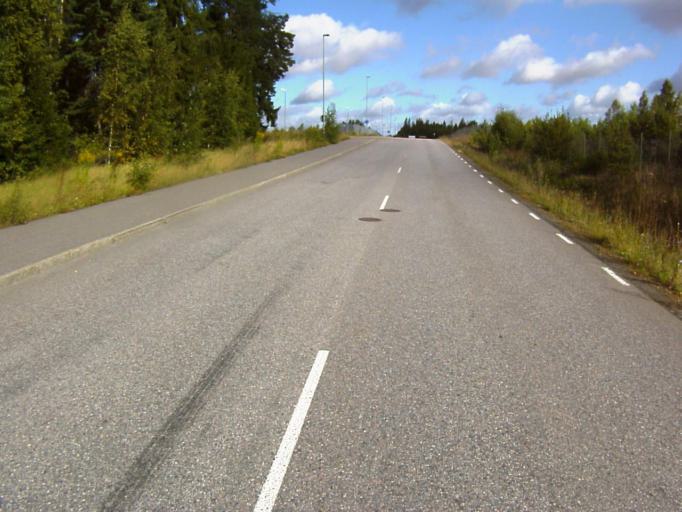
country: SE
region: Soedermanland
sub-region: Eskilstuna Kommun
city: Eskilstuna
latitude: 59.3797
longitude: 16.5934
